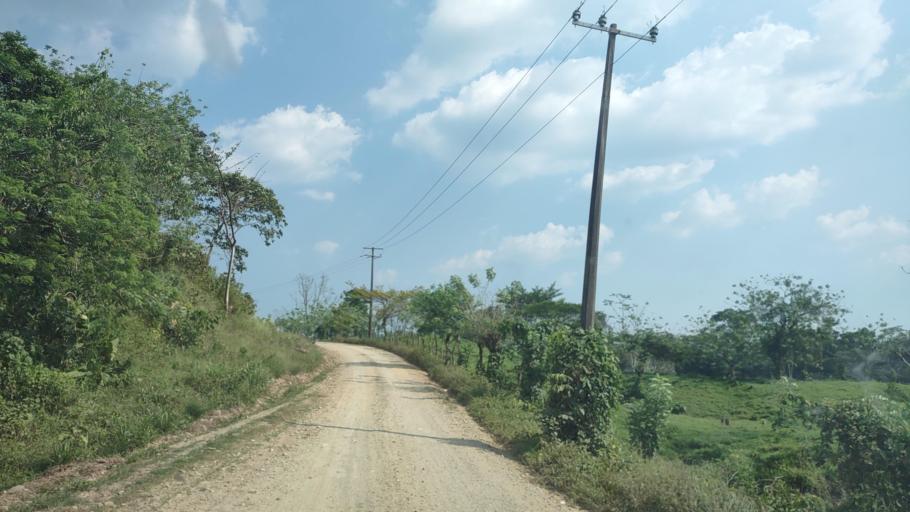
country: MX
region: Chiapas
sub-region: Tecpatan
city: Raudales Malpaso
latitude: 17.3327
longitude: -93.7506
